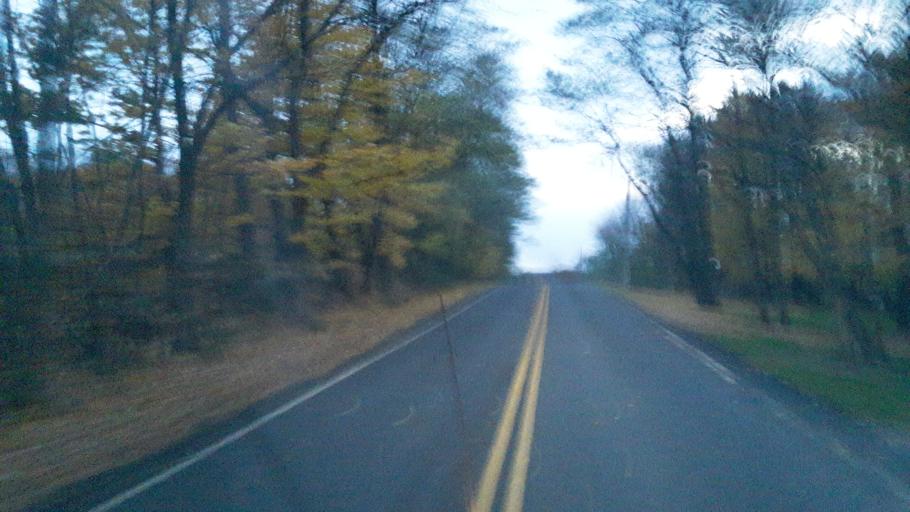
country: US
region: Ohio
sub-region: Portage County
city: Mantua
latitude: 41.3002
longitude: -81.2549
